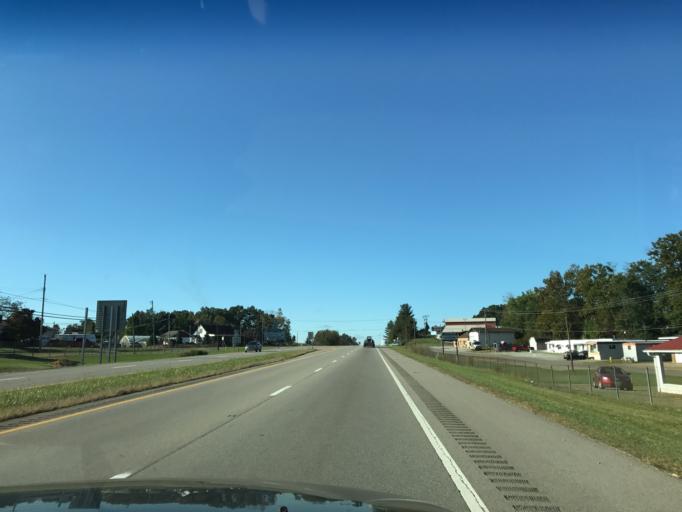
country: US
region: West Virginia
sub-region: Wood County
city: Washington
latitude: 39.2742
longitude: -81.6901
